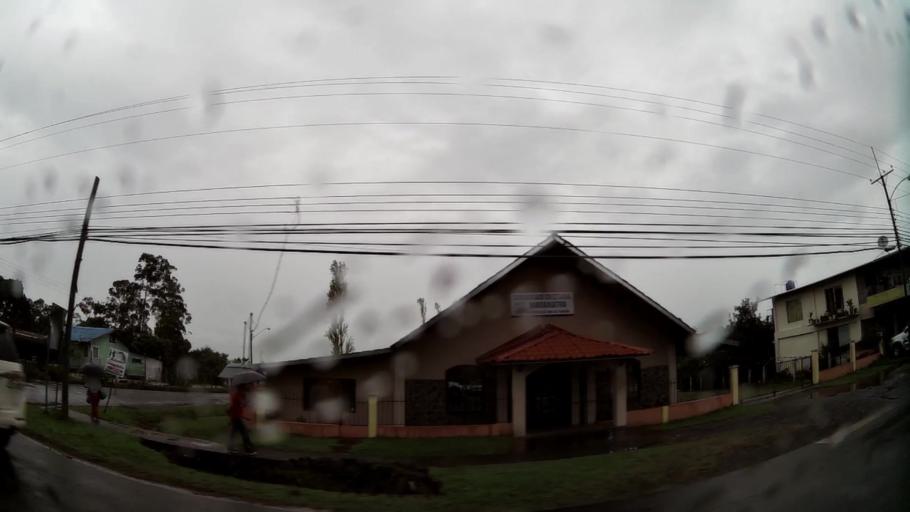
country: PA
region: Chiriqui
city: Volcan
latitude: 8.7834
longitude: -82.6483
